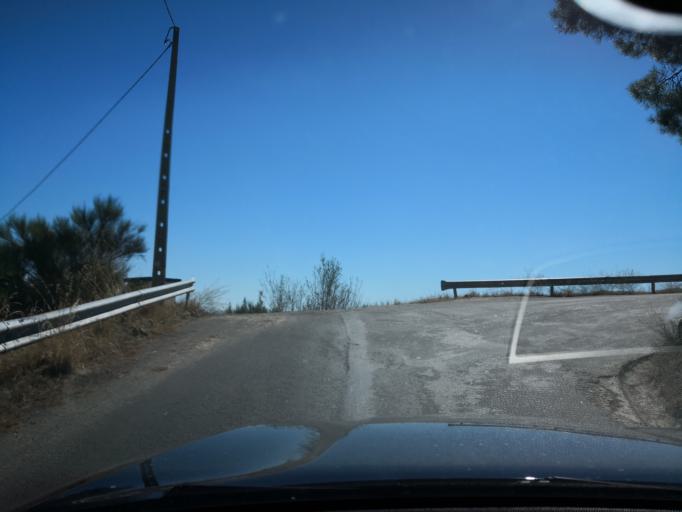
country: PT
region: Vila Real
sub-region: Vila Real
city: Vila Real
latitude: 41.2640
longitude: -7.7775
